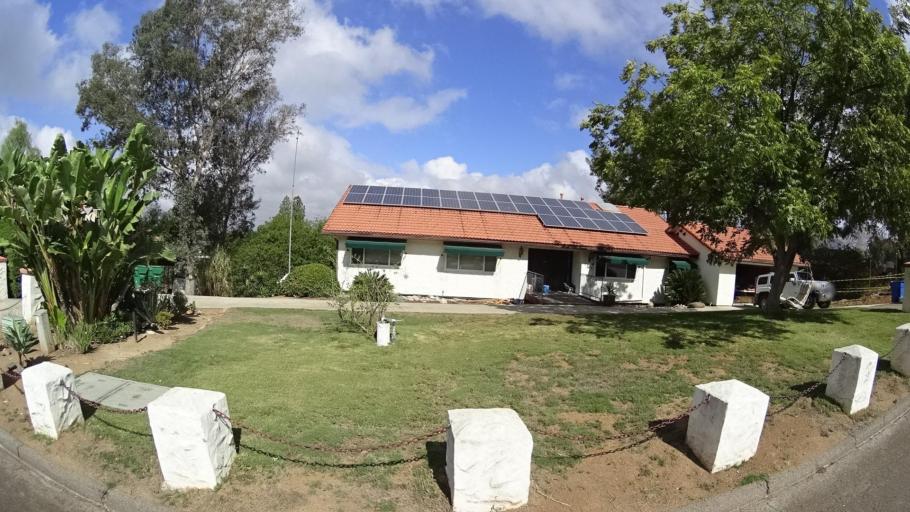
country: US
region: California
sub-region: San Diego County
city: Granite Hills
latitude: 32.7790
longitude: -116.9041
